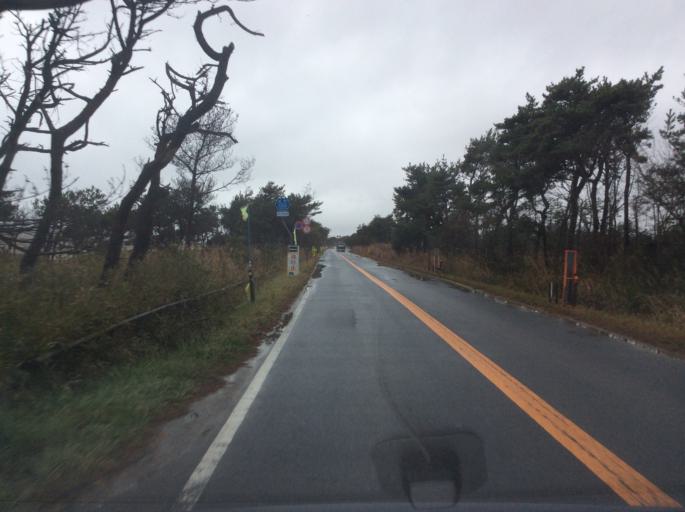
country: JP
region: Fukushima
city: Iwaki
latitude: 37.0703
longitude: 140.9768
